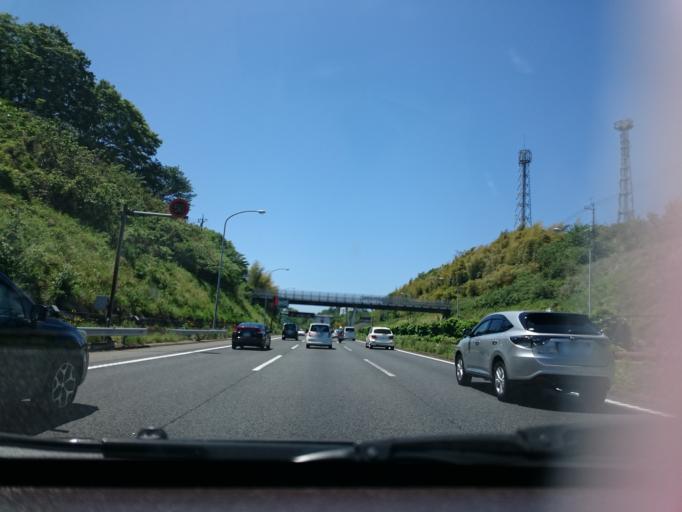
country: JP
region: Tokyo
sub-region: Machida-shi
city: Machida
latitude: 35.5150
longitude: 139.4932
